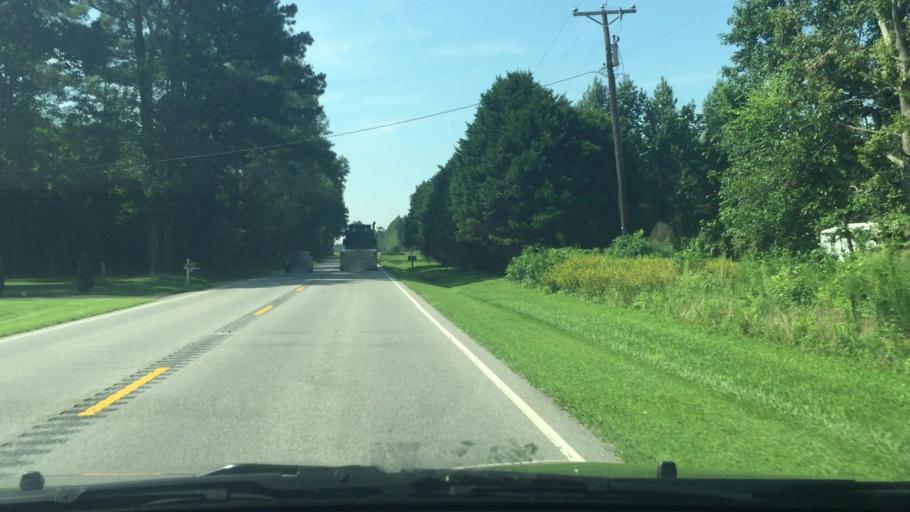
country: US
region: Virginia
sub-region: Sussex County
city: Sussex
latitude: 36.8916
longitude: -77.1533
